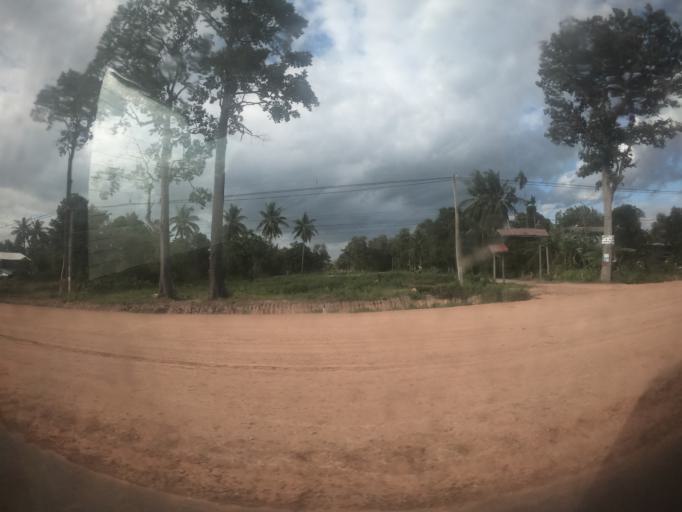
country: TH
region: Surin
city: Kap Choeng
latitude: 14.4903
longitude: 103.5745
